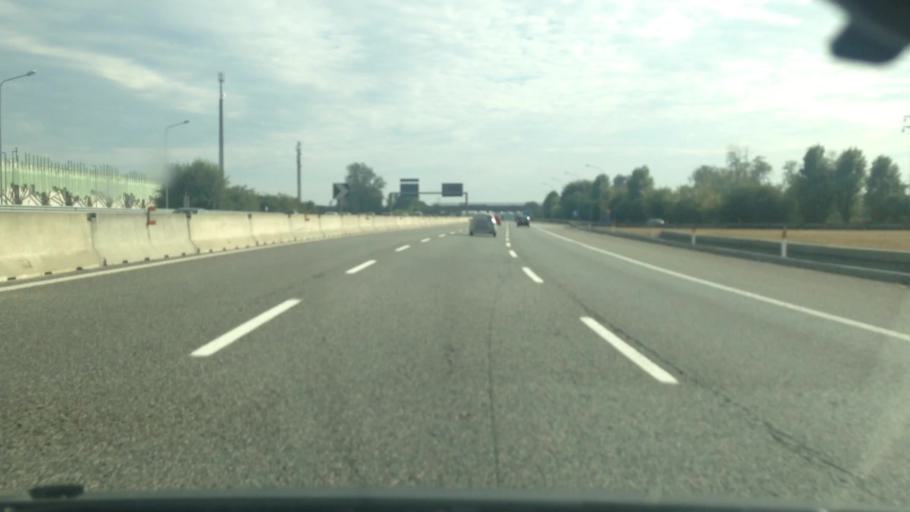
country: IT
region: Piedmont
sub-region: Provincia di Torino
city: Nichelino
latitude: 45.0063
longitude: 7.6207
